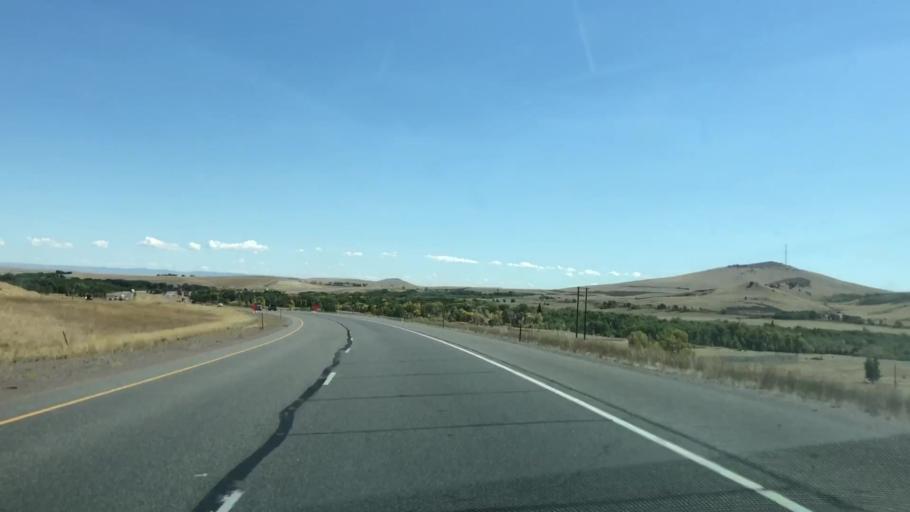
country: US
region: Wyoming
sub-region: Carbon County
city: Saratoga
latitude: 41.5980
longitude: -106.2185
